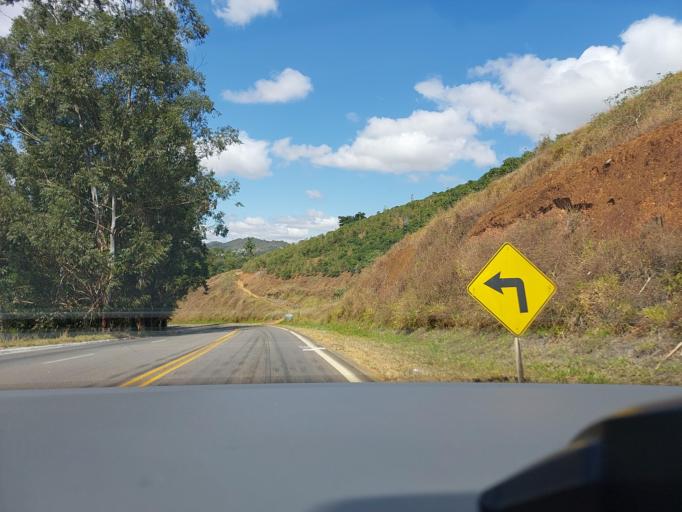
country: BR
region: Minas Gerais
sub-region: Mirai
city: Mirai
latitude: -21.0420
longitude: -42.5321
